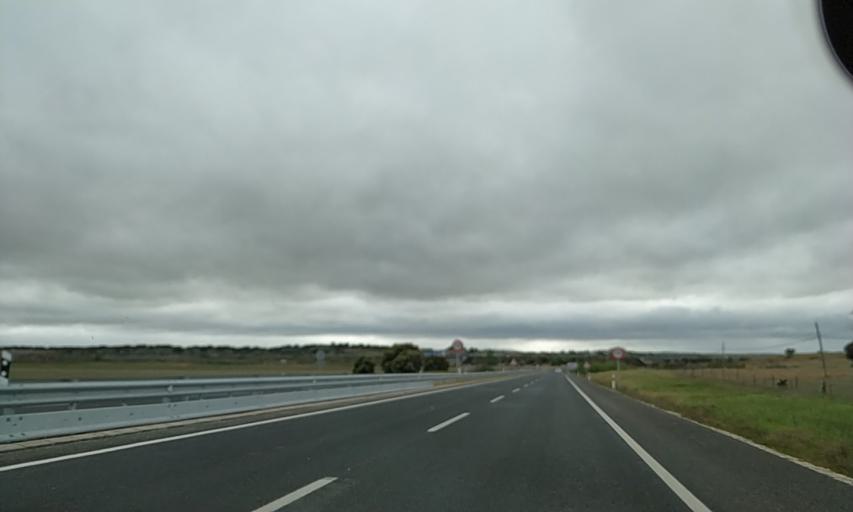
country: ES
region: Extremadura
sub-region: Provincia de Caceres
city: Caceres
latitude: 39.4626
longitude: -6.4148
